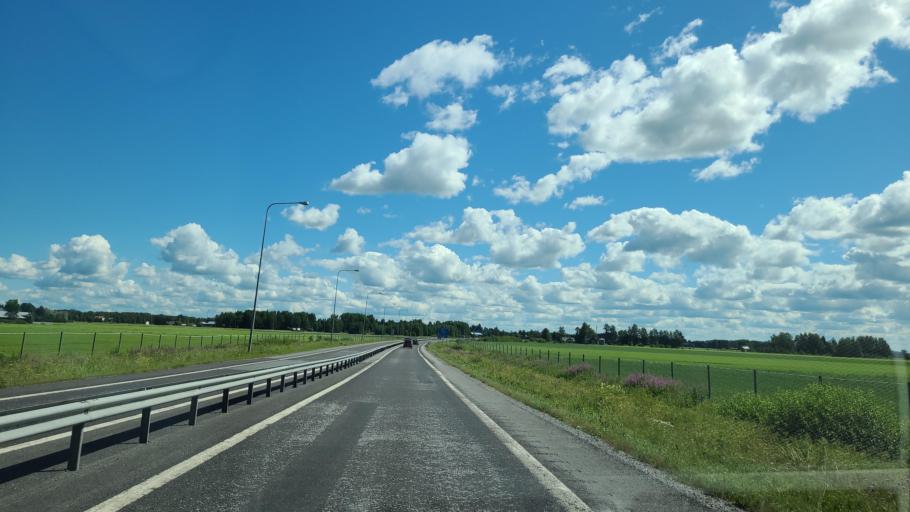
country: FI
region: Ostrobothnia
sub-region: Vaasa
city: Ristinummi
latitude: 63.0250
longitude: 21.7797
